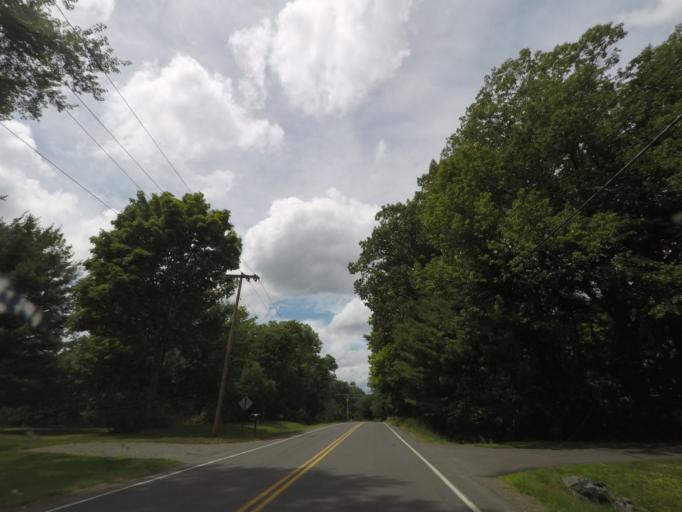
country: US
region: New York
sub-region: Rensselaer County
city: Wynantskill
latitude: 42.7087
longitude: -73.6512
